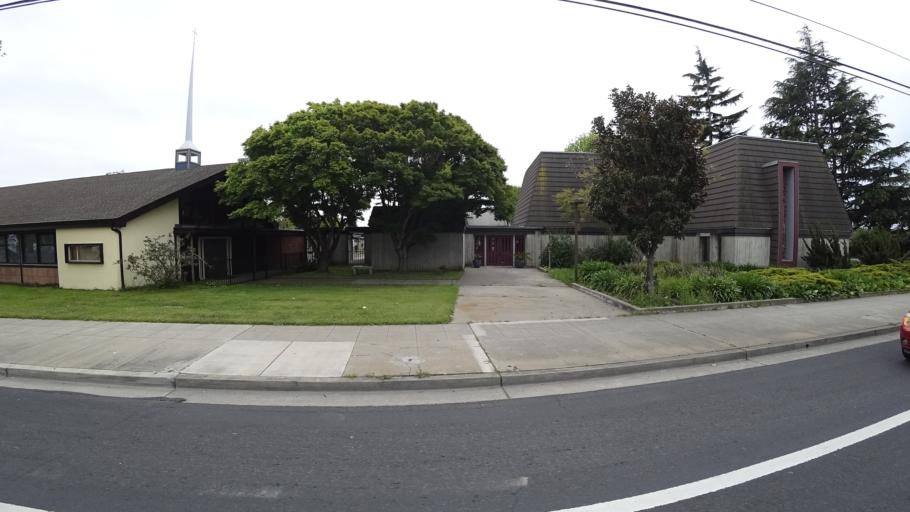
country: US
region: California
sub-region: Alameda County
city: Hayward
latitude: 37.6485
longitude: -122.0825
